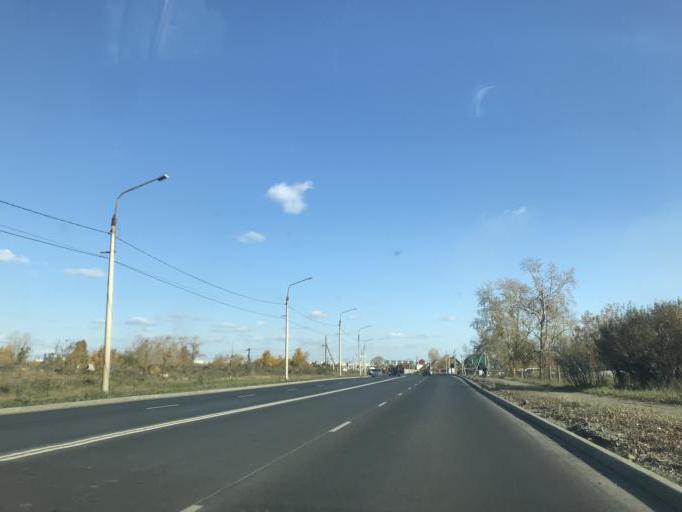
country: RU
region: Chelyabinsk
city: Dolgoderevenskoye
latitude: 55.2399
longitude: 61.3414
